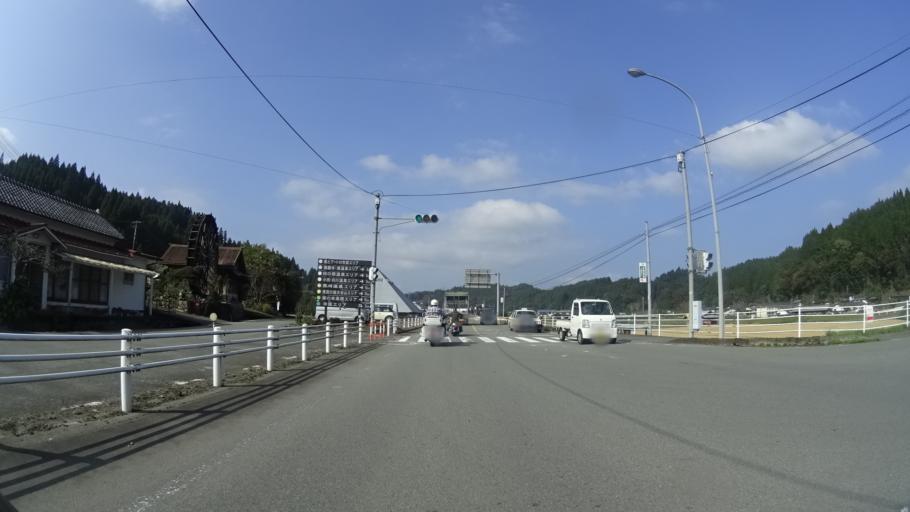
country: JP
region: Kumamoto
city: Aso
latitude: 33.0988
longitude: 131.0682
